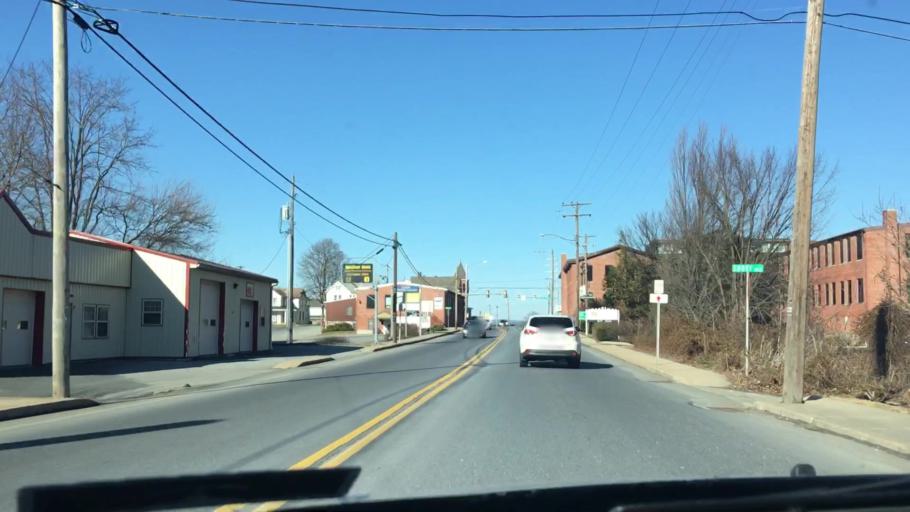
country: US
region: Pennsylvania
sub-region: Lancaster County
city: Akron
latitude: 40.1562
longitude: -76.2053
